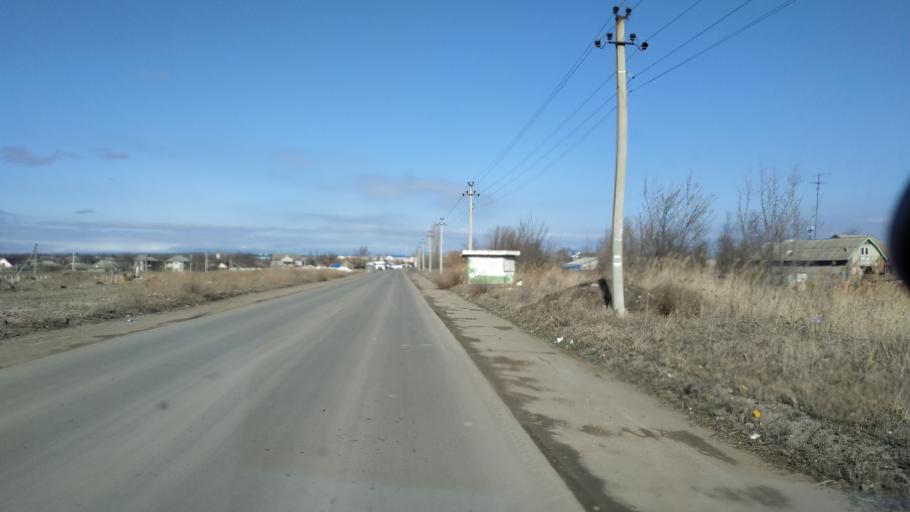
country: MD
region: Causeni
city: Causeni
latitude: 46.6450
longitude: 29.4050
